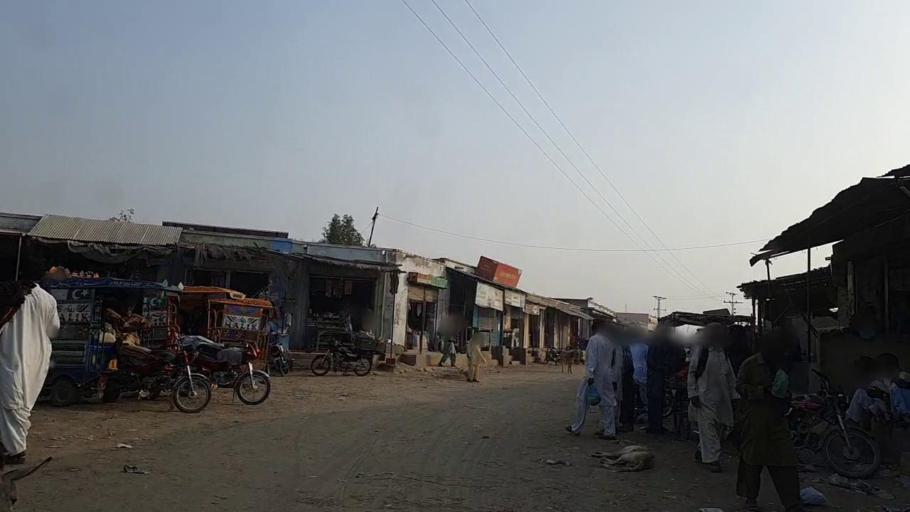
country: PK
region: Sindh
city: Naukot
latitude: 24.6564
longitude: 69.2906
